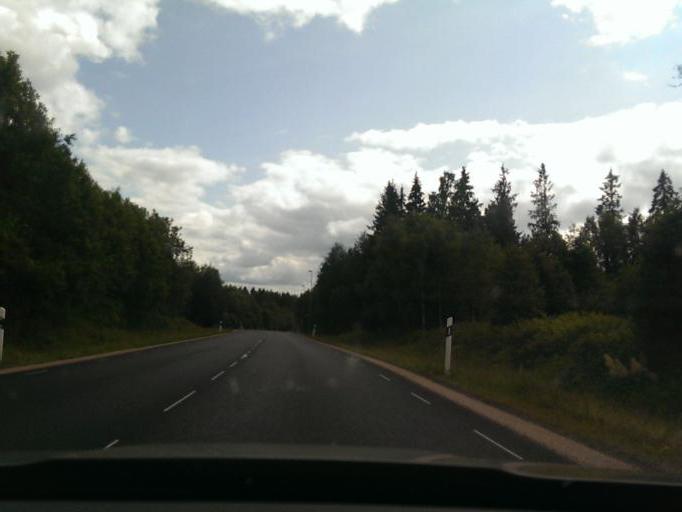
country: SE
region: Joenkoeping
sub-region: Varnamo Kommun
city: Varnamo
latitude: 57.1891
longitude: 14.0080
